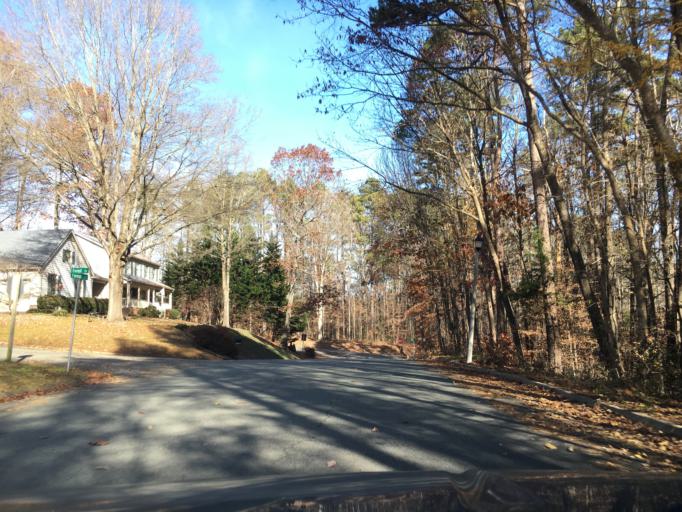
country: US
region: Virginia
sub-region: Halifax County
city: South Boston
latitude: 36.7093
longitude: -78.9144
